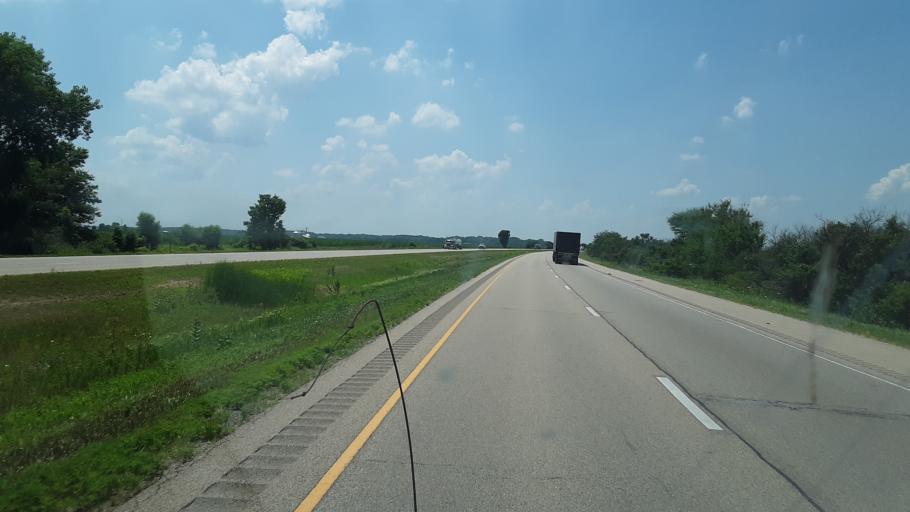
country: US
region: Illinois
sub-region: Bureau County
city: Princeton
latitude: 41.3875
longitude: -89.5258
